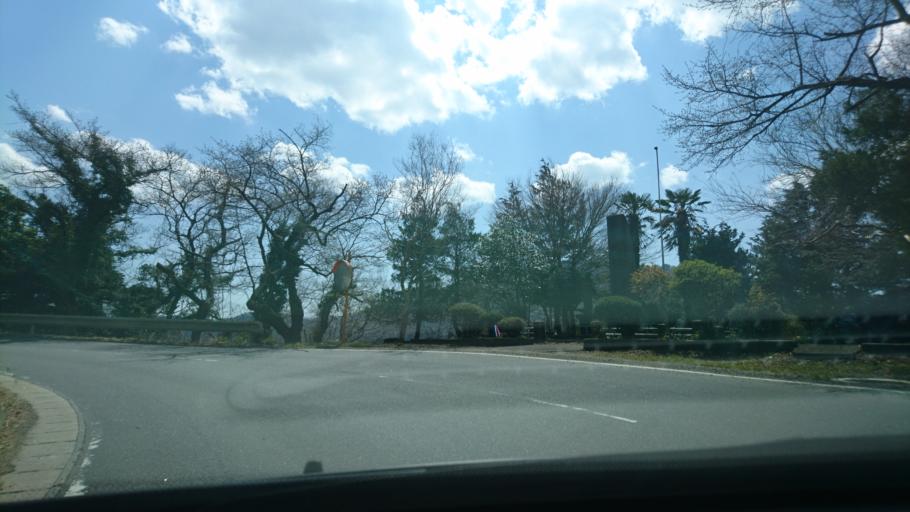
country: JP
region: Miyagi
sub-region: Oshika Gun
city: Onagawa Cho
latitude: 38.4421
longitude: 141.4654
